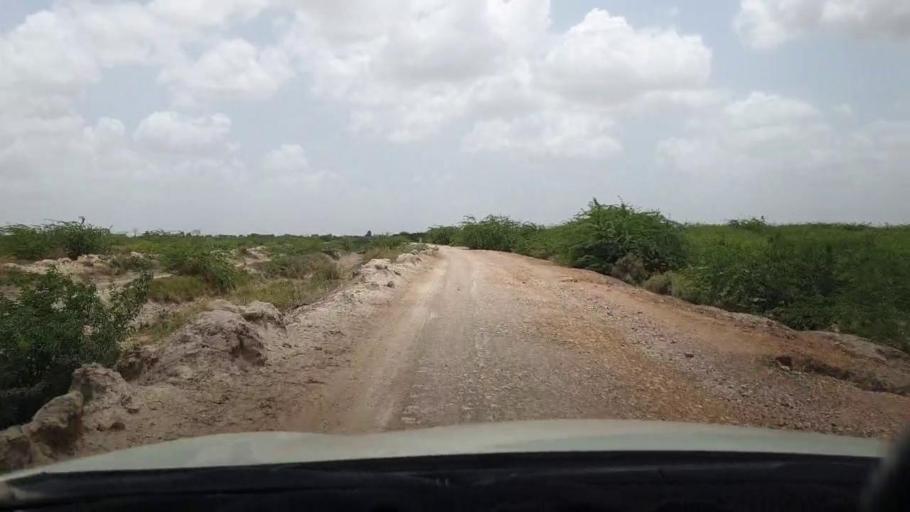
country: PK
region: Sindh
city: Kadhan
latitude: 24.3847
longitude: 68.9319
